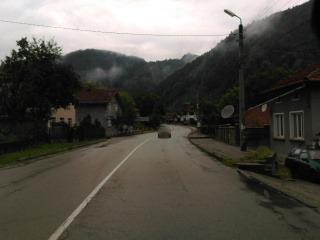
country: BG
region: Lovech
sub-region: Obshtina Troyan
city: Troyan
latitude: 42.8642
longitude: 24.6982
